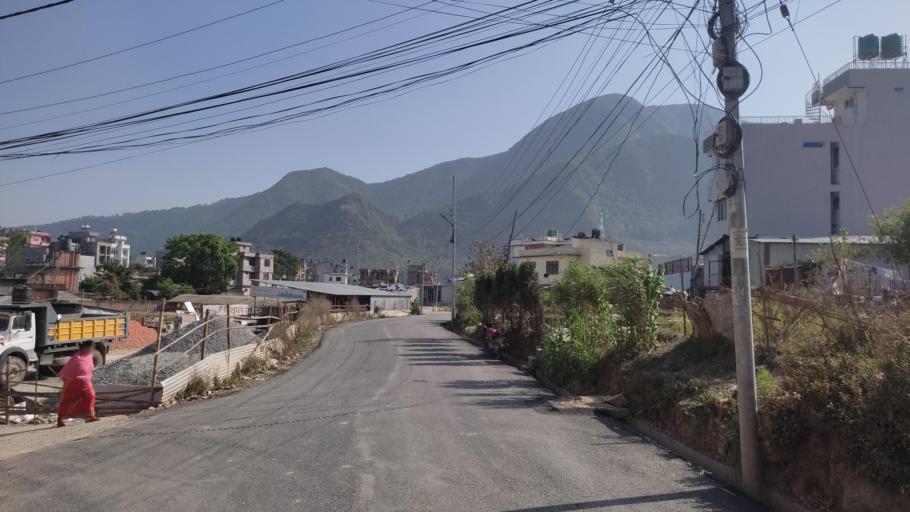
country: NP
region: Central Region
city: Kirtipur
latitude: 27.6688
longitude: 85.2713
